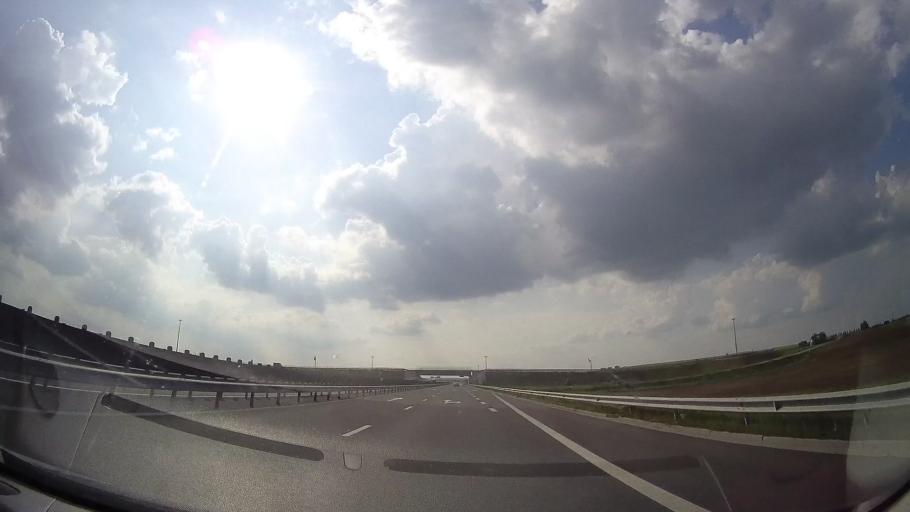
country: RO
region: Timis
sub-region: Comuna Manastiur
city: Manastiur
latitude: 45.8117
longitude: 22.0757
